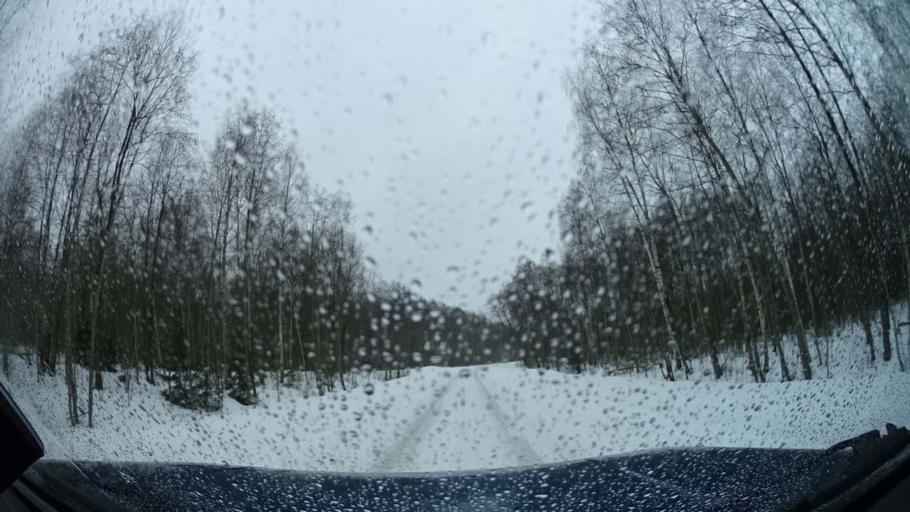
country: RU
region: Tverskaya
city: Radchenko
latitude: 56.7682
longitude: 36.5053
